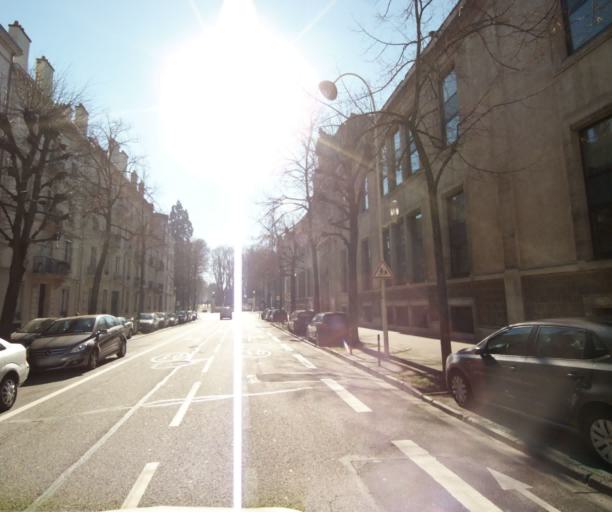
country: FR
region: Lorraine
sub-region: Departement de Meurthe-et-Moselle
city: Malzeville
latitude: 48.6999
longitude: 6.1801
